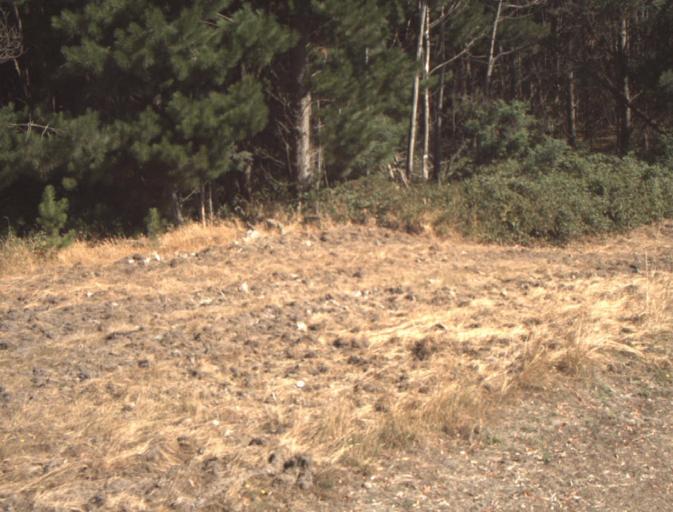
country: AU
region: Tasmania
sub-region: Launceston
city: Mayfield
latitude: -41.1689
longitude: 147.2115
